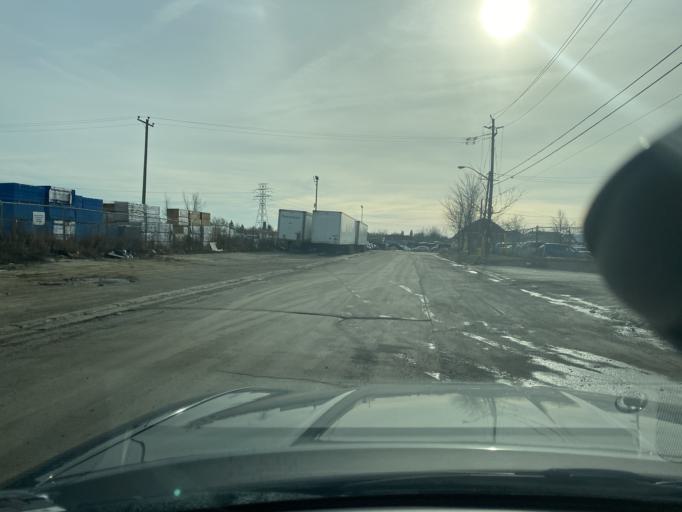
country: CA
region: Ontario
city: Scarborough
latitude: 43.7219
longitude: -79.2780
